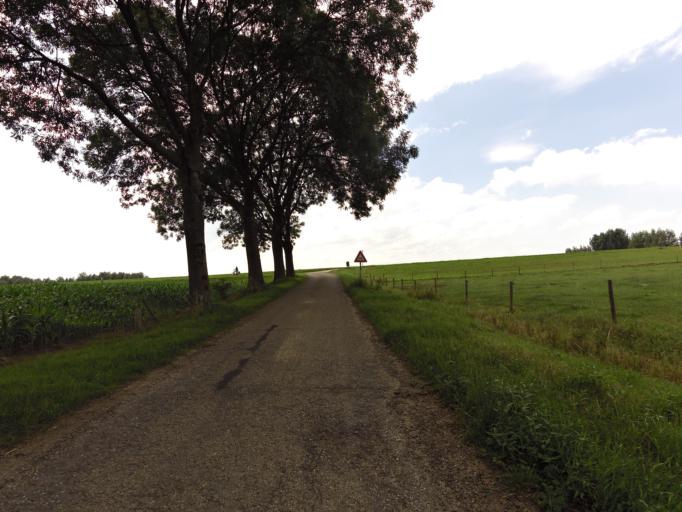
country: NL
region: Gelderland
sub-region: Gemeente Doesburg
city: Doesburg
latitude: 52.0241
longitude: 6.1597
